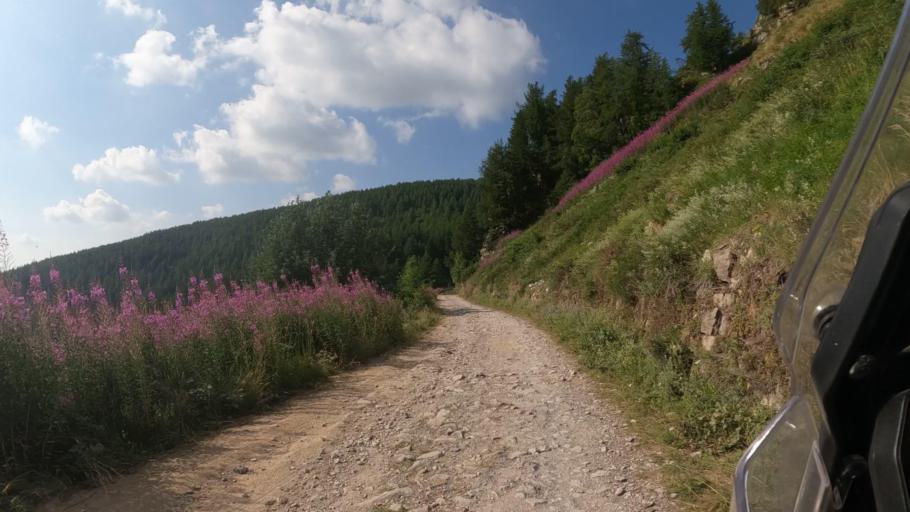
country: IT
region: Piedmont
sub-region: Provincia di Cuneo
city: Briga Alta
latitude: 44.1242
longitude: 7.6907
